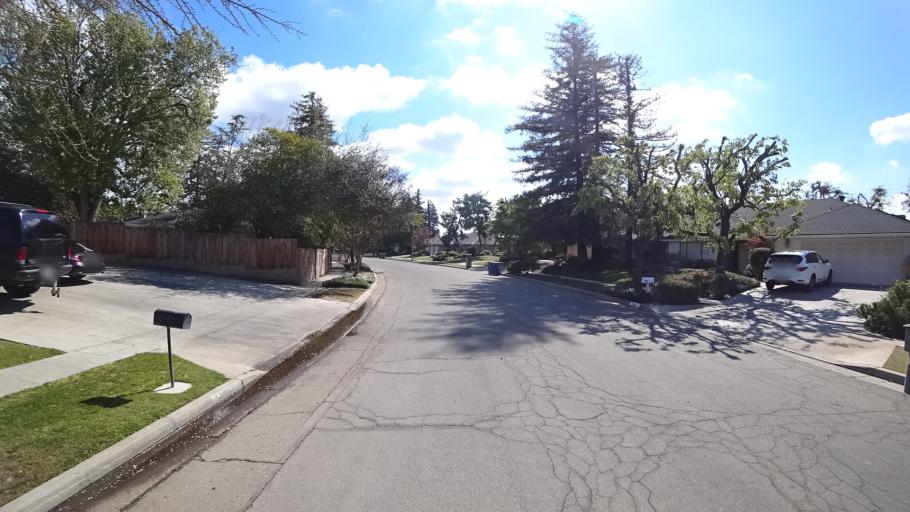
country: US
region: California
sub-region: Fresno County
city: Fresno
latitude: 36.8273
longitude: -119.8482
